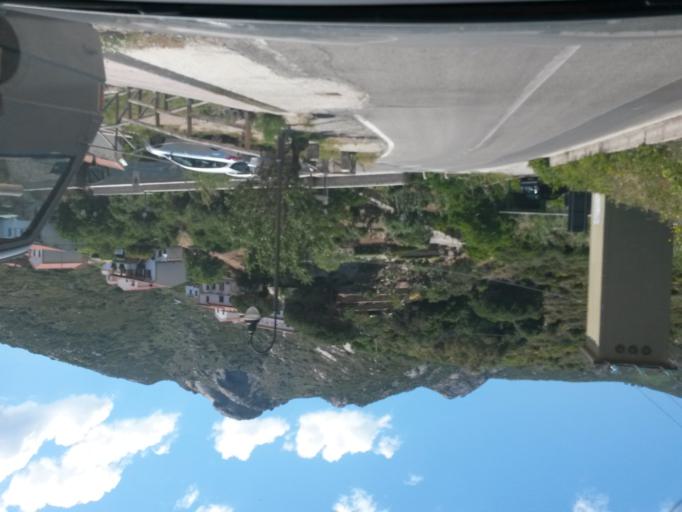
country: IT
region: Tuscany
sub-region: Provincia di Livorno
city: Marciana
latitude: 42.7606
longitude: 10.1116
